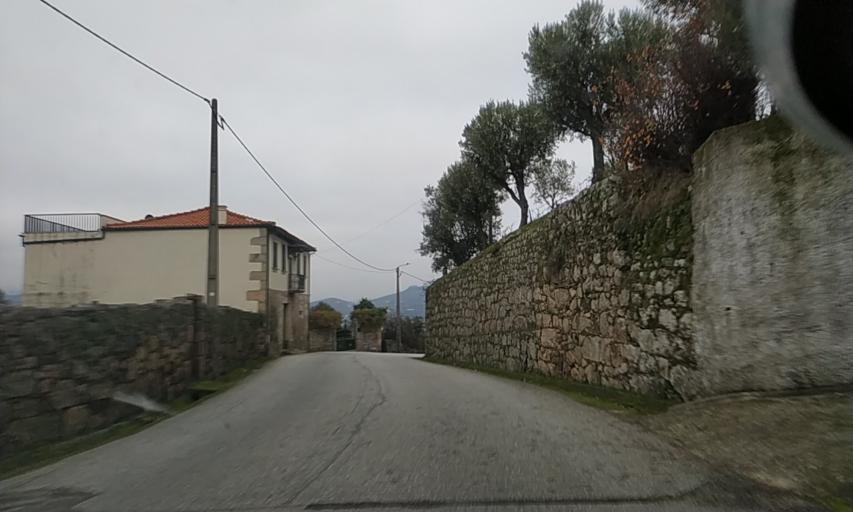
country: PT
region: Vila Real
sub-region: Peso da Regua
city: Peso da Regua
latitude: 41.1356
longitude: -7.7945
